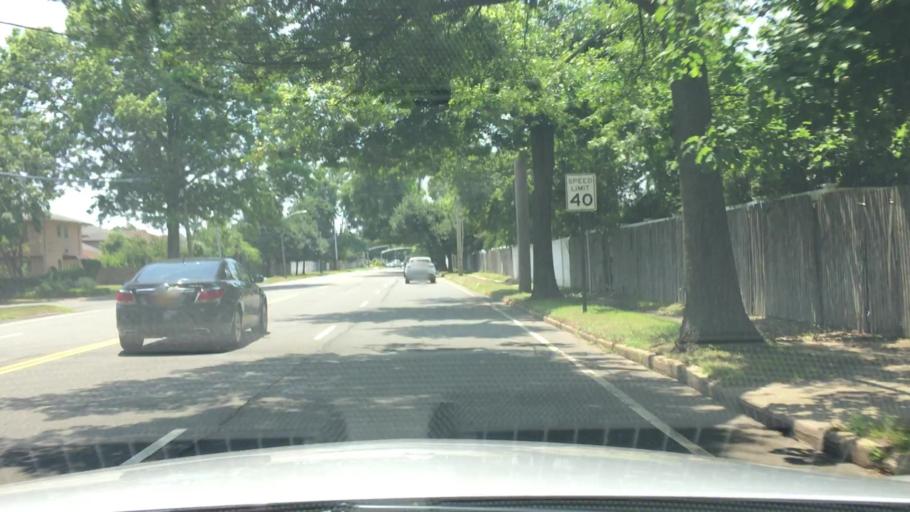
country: US
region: New York
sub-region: Nassau County
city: Plainview
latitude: 40.7881
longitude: -73.4965
